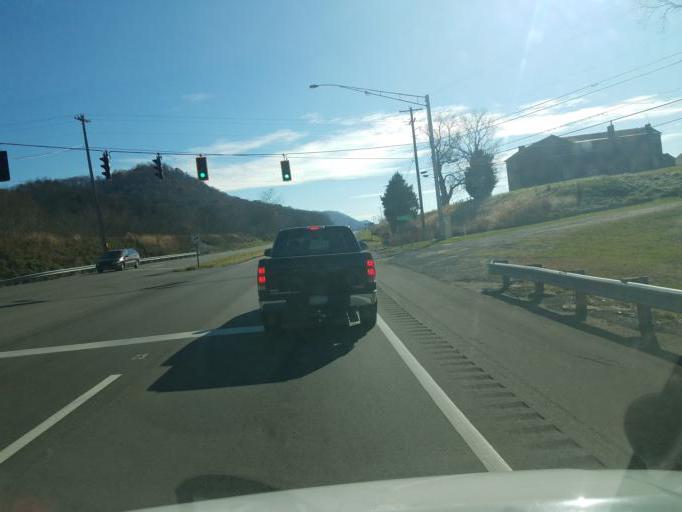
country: US
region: Ohio
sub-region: Scioto County
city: Lucasville
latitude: 38.8413
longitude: -82.9845
